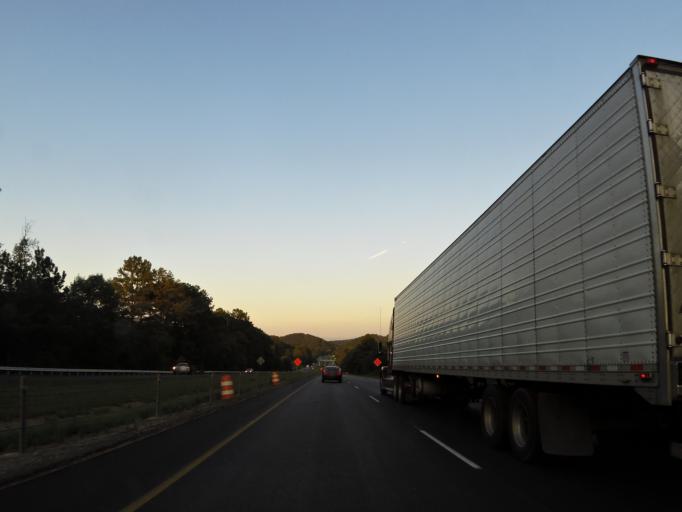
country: US
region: Tennessee
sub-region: Roane County
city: Kingston
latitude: 35.8724
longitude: -84.4767
